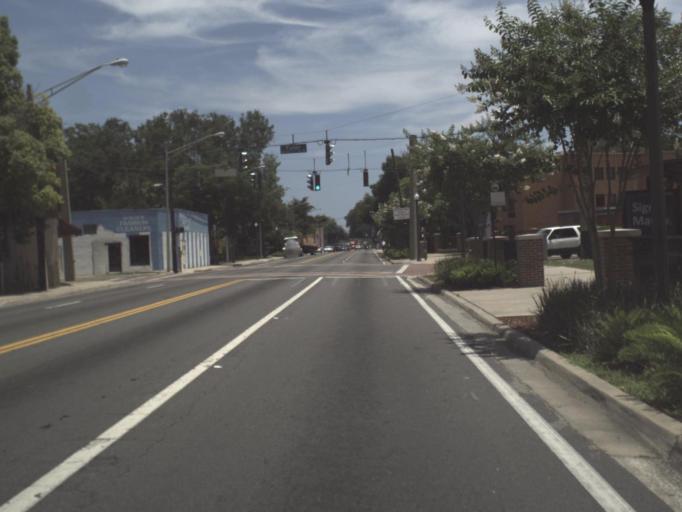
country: US
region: Florida
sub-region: Duval County
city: Jacksonville
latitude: 30.3435
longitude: -81.6827
